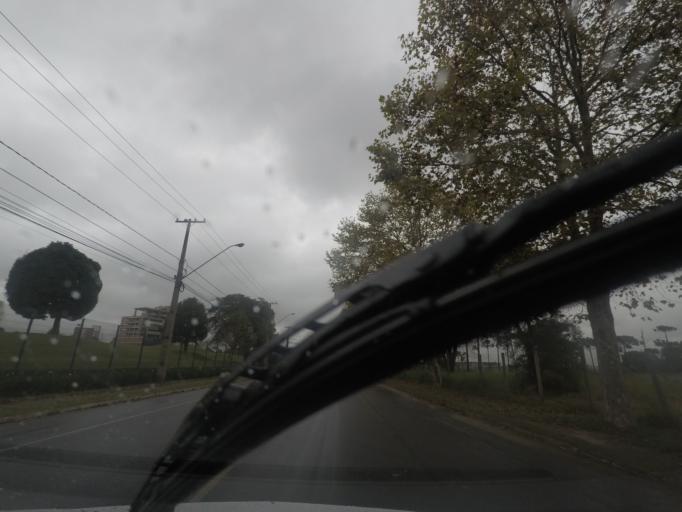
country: BR
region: Parana
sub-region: Pinhais
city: Pinhais
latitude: -25.3913
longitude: -49.1588
